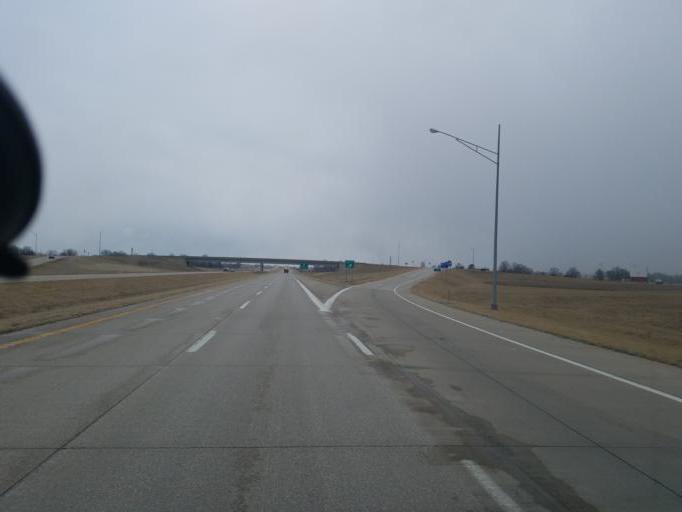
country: US
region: Missouri
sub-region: Randolph County
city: Moberly
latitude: 39.4571
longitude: -92.4335
